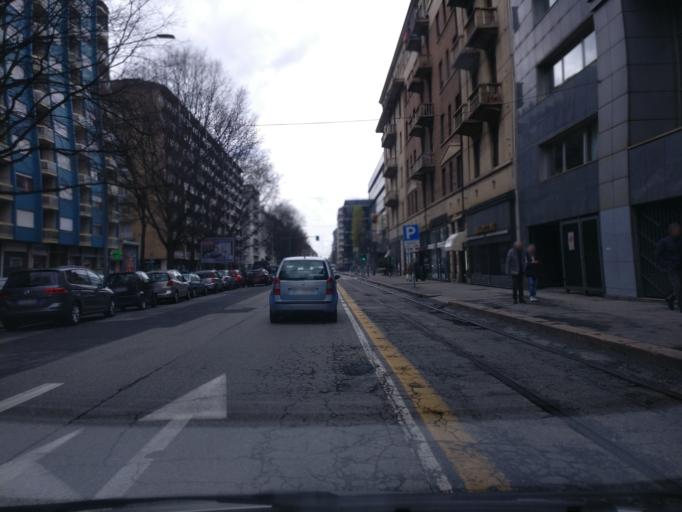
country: IT
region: Piedmont
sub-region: Provincia di Torino
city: Turin
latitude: 45.0413
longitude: 7.6707
